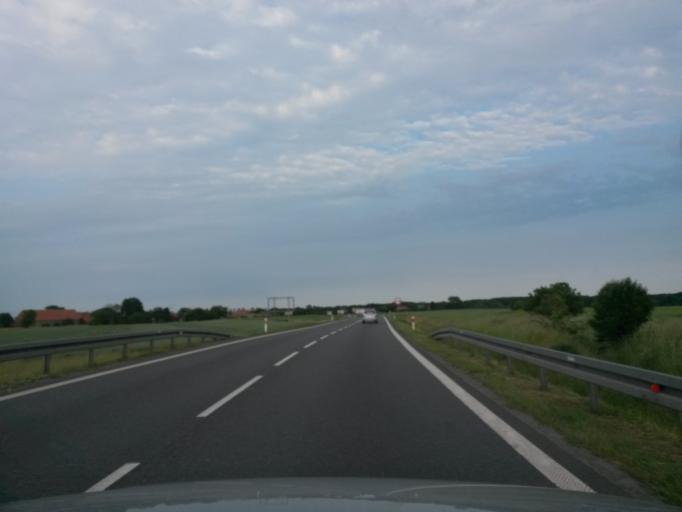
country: PL
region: Lower Silesian Voivodeship
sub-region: Powiat swidnicki
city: Zarow
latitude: 51.0069
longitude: 16.5394
